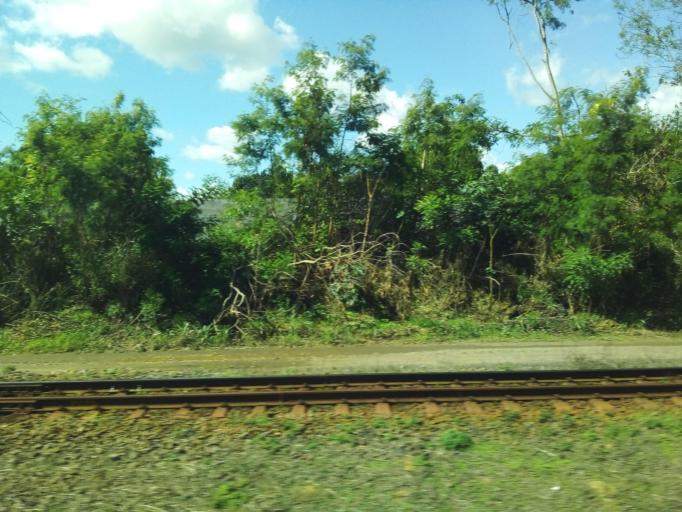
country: BR
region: Minas Gerais
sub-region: Governador Valadares
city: Governador Valadares
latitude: -18.8387
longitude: -41.8794
